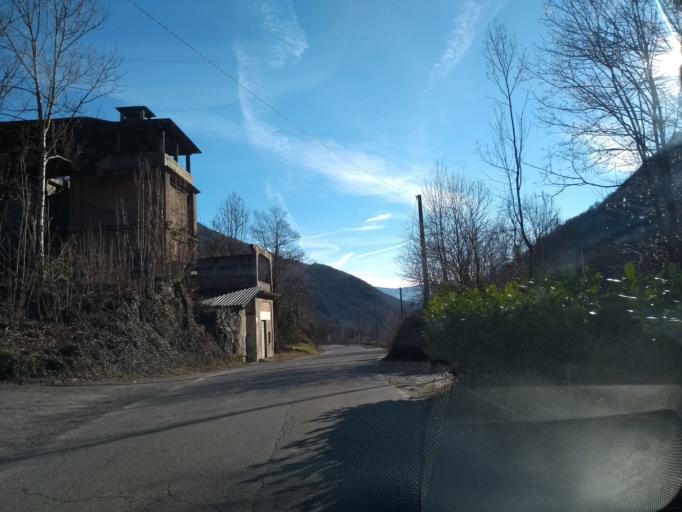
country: IT
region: Piedmont
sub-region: Provincia di Torino
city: Cantoira
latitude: 45.3357
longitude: 7.3880
